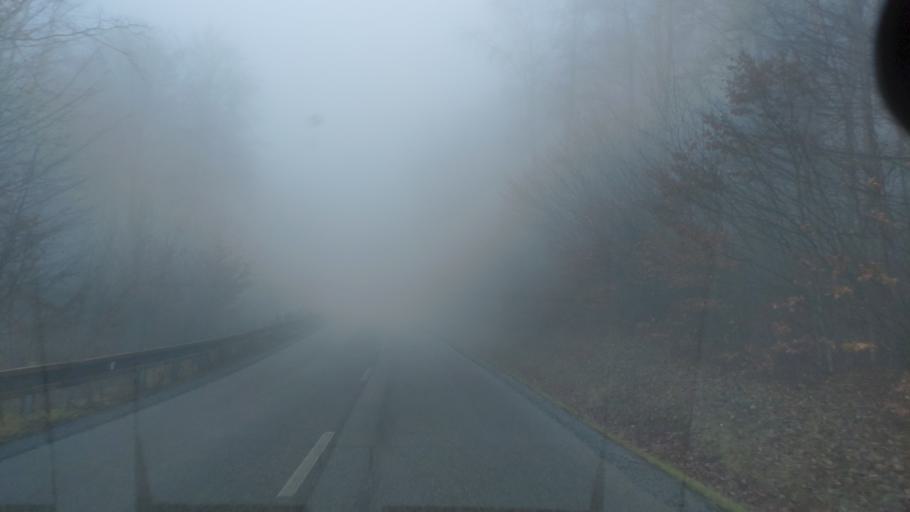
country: SK
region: Banskobystricky
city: Revuca
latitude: 48.6317
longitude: 20.2887
